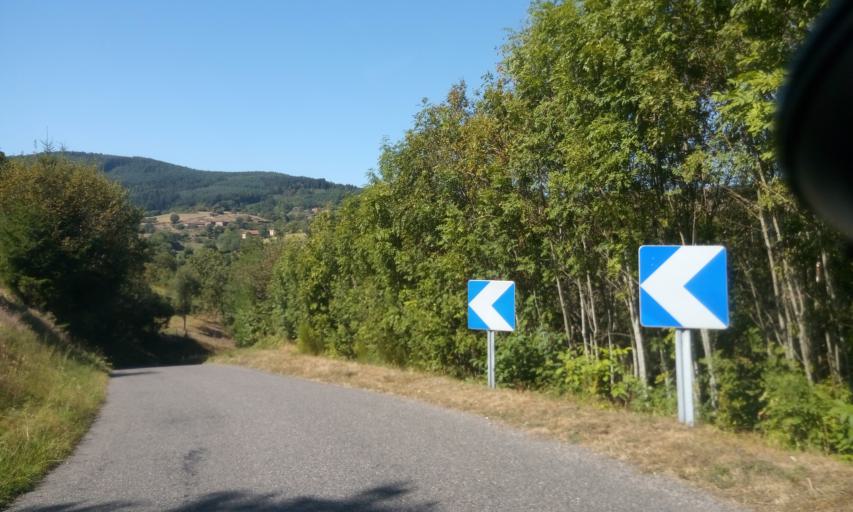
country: FR
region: Rhone-Alpes
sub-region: Departement du Rhone
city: Grandris
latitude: 46.0028
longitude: 4.4535
